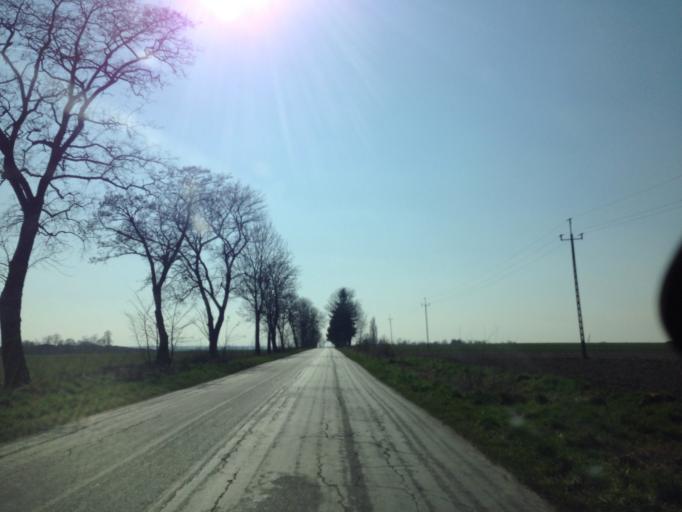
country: PL
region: Lower Silesian Voivodeship
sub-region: Powiat olesnicki
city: Bierutow
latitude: 51.1962
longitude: 17.5329
